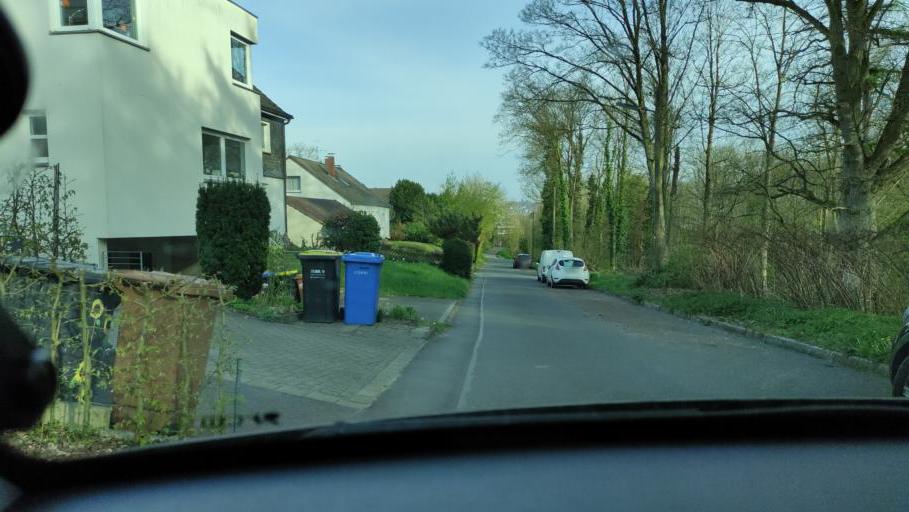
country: DE
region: North Rhine-Westphalia
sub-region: Regierungsbezirk Dusseldorf
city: Essen
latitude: 51.4094
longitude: 7.0674
